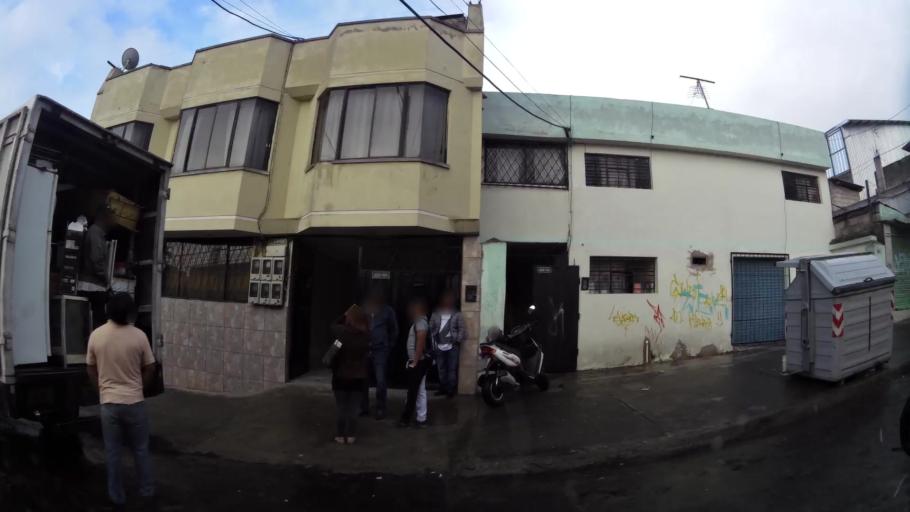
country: EC
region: Pichincha
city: Quito
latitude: -0.1069
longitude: -78.4953
